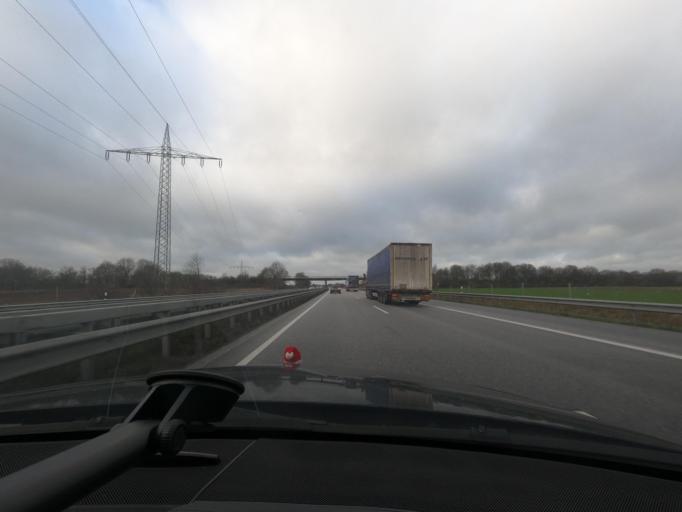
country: DE
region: Schleswig-Holstein
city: Hassmoor
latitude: 54.2589
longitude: 9.8002
